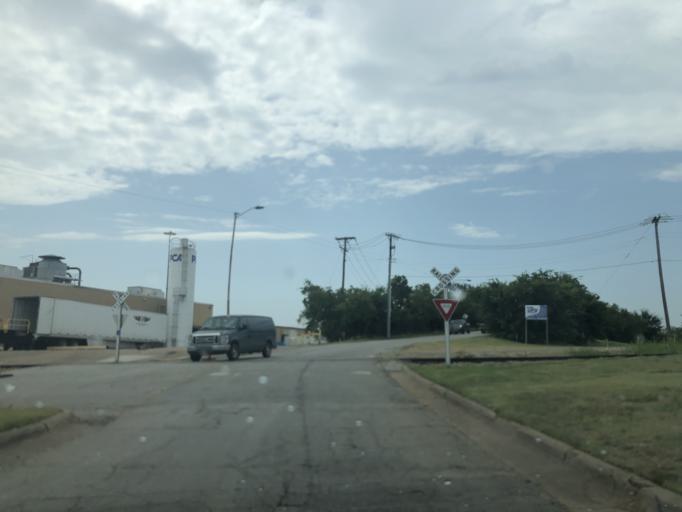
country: US
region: Texas
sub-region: Dallas County
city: Grand Prairie
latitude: 32.7615
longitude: -97.0458
